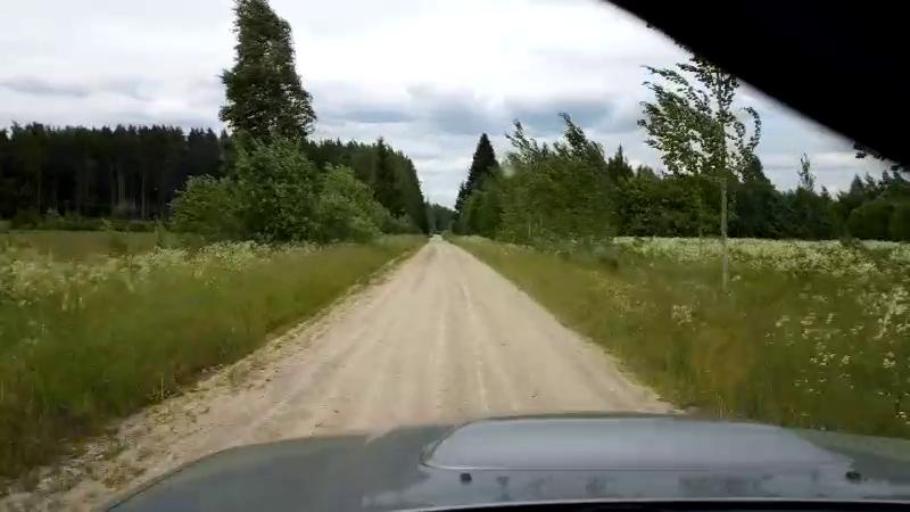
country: EE
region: Paernumaa
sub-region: Sauga vald
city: Sauga
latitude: 58.5010
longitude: 24.5807
